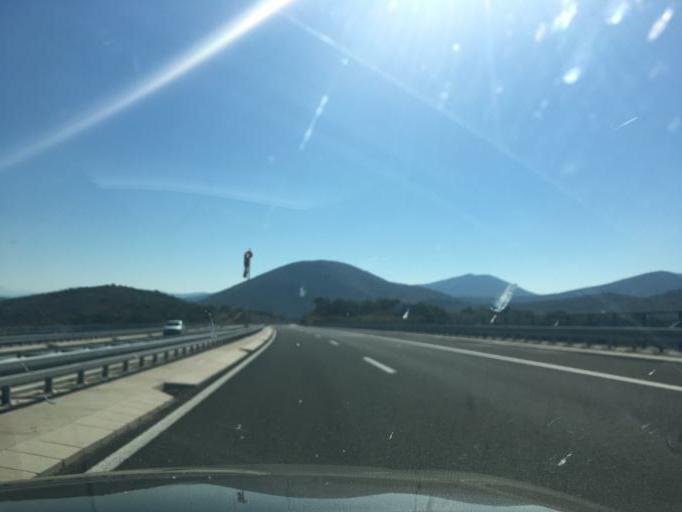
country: HR
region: Splitsko-Dalmatinska
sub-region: Grad Trogir
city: Trogir
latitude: 43.6445
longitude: 16.2025
